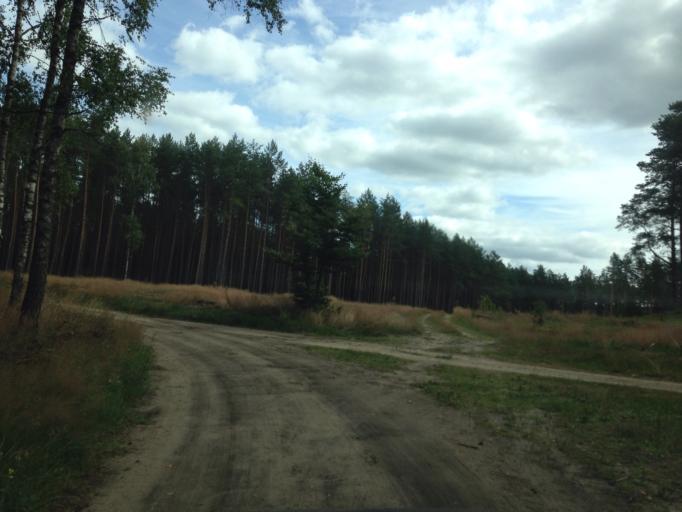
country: PL
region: Pomeranian Voivodeship
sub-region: Powiat koscierski
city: Dziemiany
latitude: 54.0615
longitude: 17.6791
